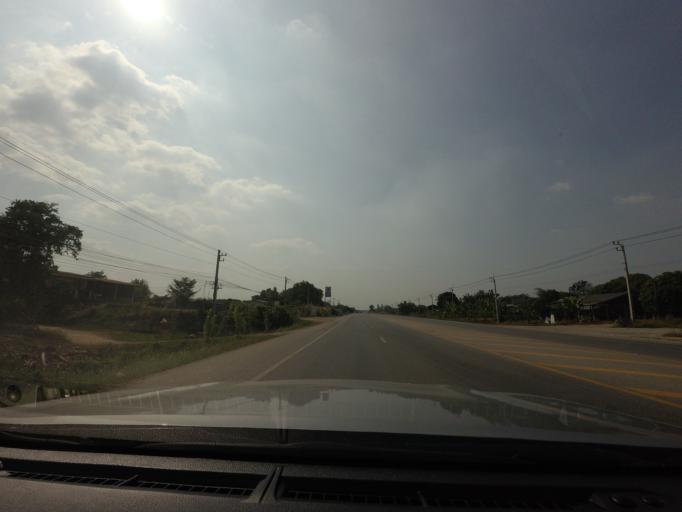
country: TH
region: Phitsanulok
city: Bang Rakam
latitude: 16.7663
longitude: 100.1391
